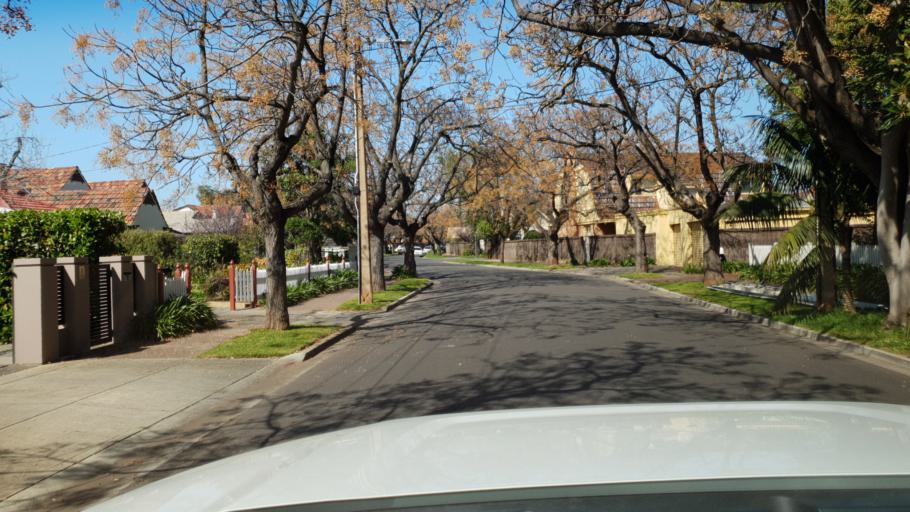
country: AU
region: South Australia
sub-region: Adelaide
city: Brighton
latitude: -35.0144
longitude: 138.5170
